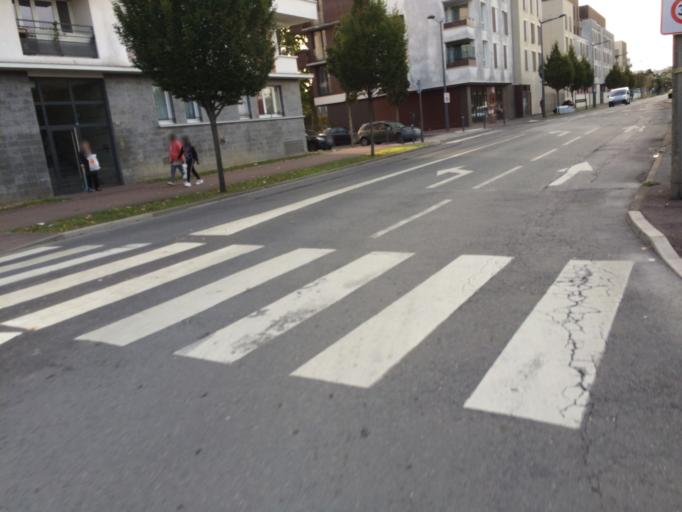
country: FR
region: Ile-de-France
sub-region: Departement de l'Essonne
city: Vigneux-sur-Seine
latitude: 48.7063
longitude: 2.4229
